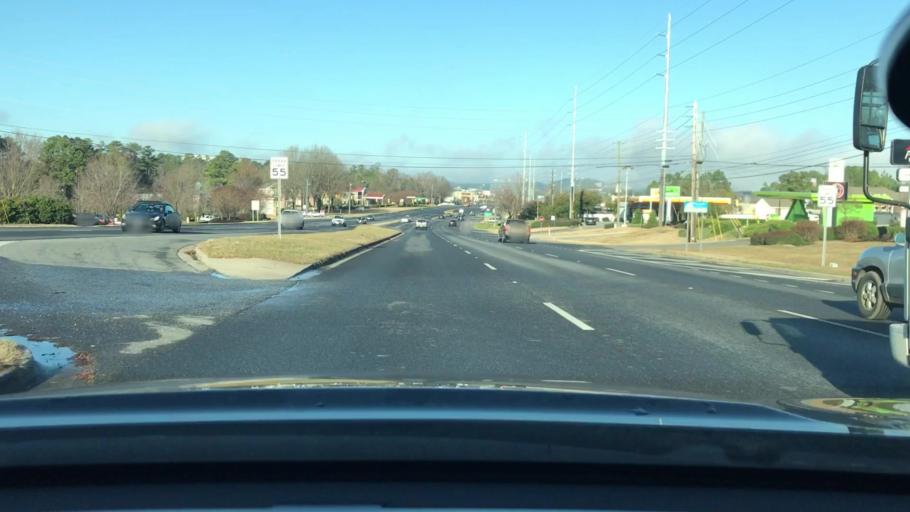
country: US
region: Alabama
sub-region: Shelby County
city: Lake Purdy
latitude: 33.4218
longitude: -86.6979
